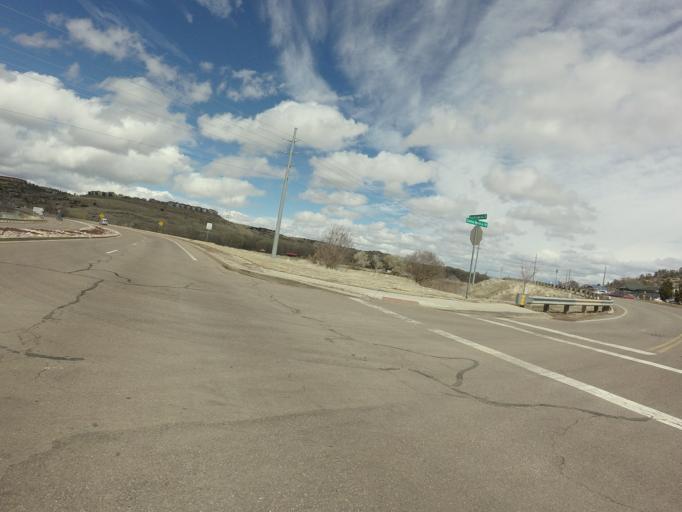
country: US
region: Arizona
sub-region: Yavapai County
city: Prescott
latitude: 34.5736
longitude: -112.4279
